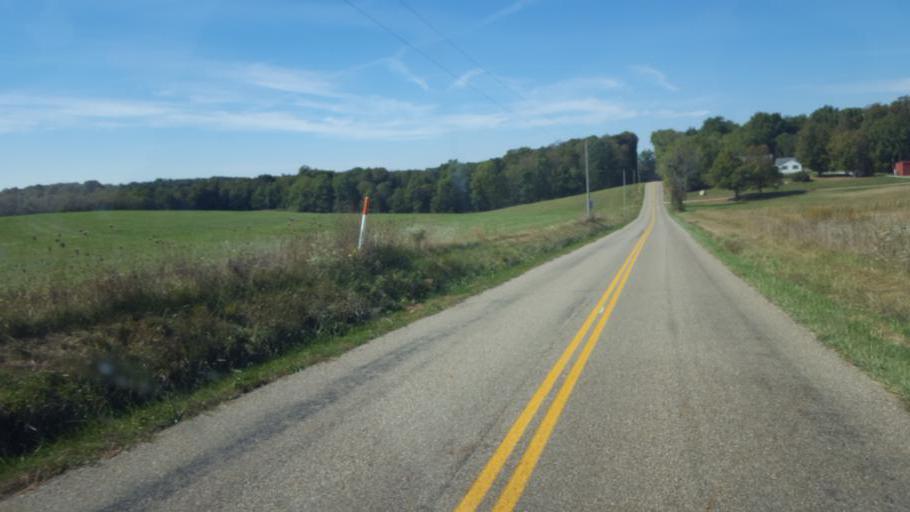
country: US
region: Ohio
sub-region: Sandusky County
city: Bellville
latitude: 40.5395
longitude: -82.4505
